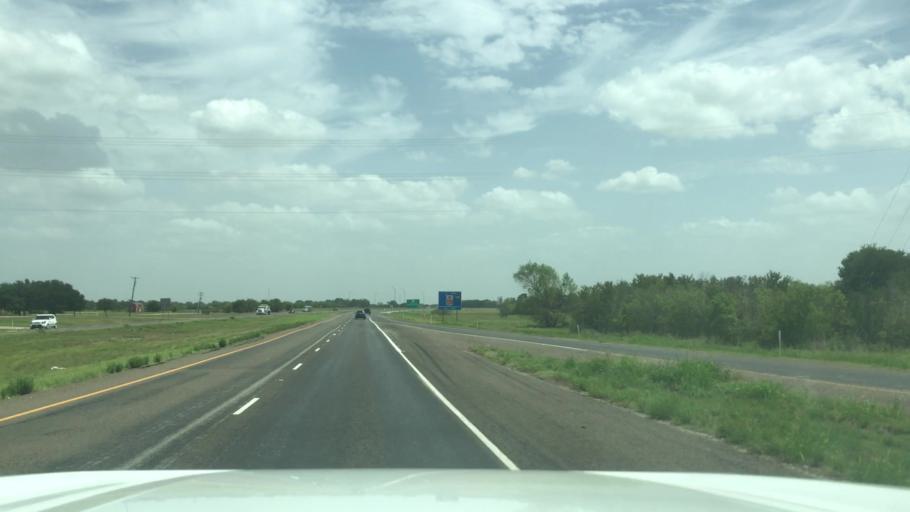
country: US
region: Texas
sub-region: Falls County
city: Marlin
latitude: 31.3182
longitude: -96.8800
